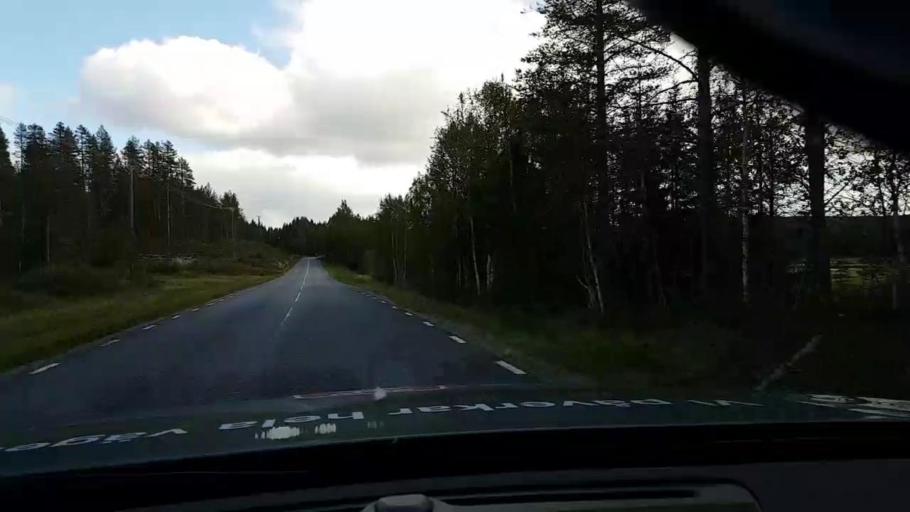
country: SE
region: Vaesterbotten
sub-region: Asele Kommun
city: Asele
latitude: 63.8091
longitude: 17.5326
